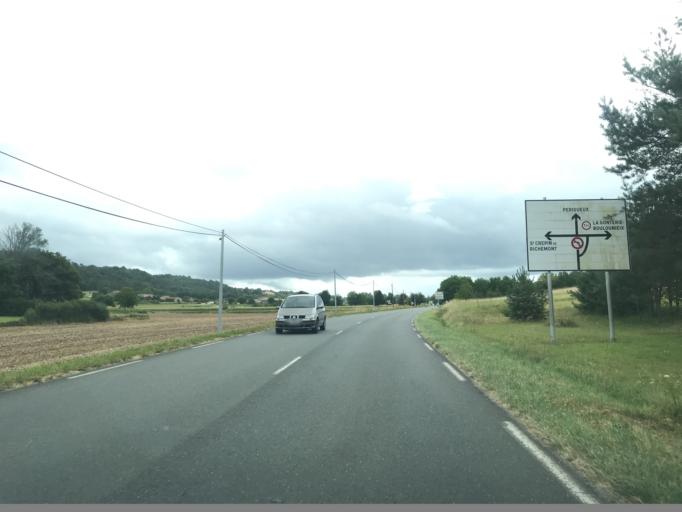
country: FR
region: Aquitaine
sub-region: Departement de la Dordogne
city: Brantome
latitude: 45.4065
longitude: 0.5881
